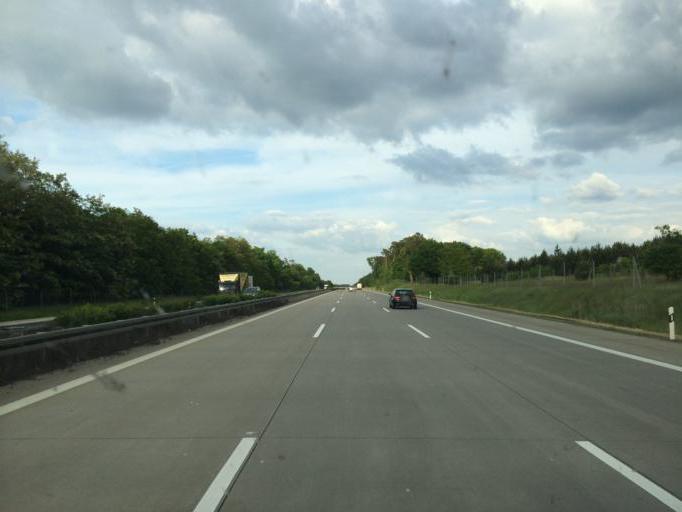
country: DE
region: Saxony-Anhalt
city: Tucheim
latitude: 52.2450
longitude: 12.1541
